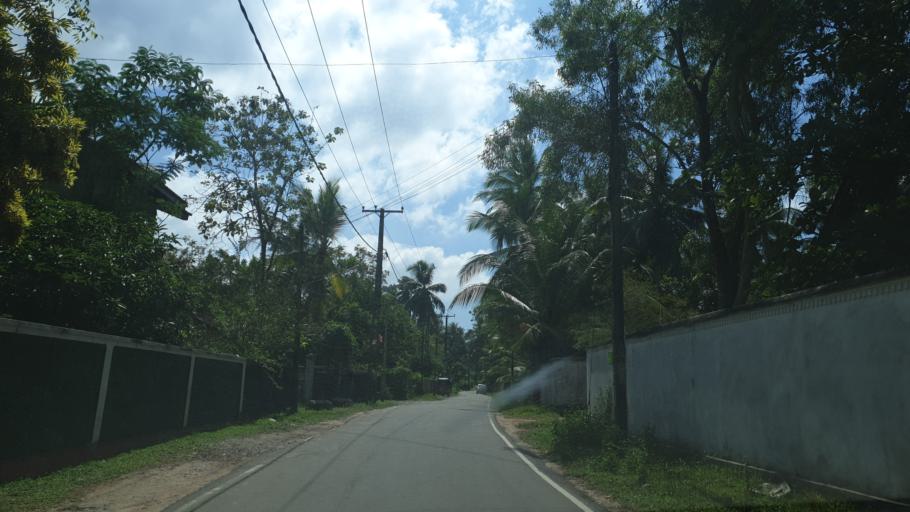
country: LK
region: Western
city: Panadura
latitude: 6.6804
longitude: 79.9297
